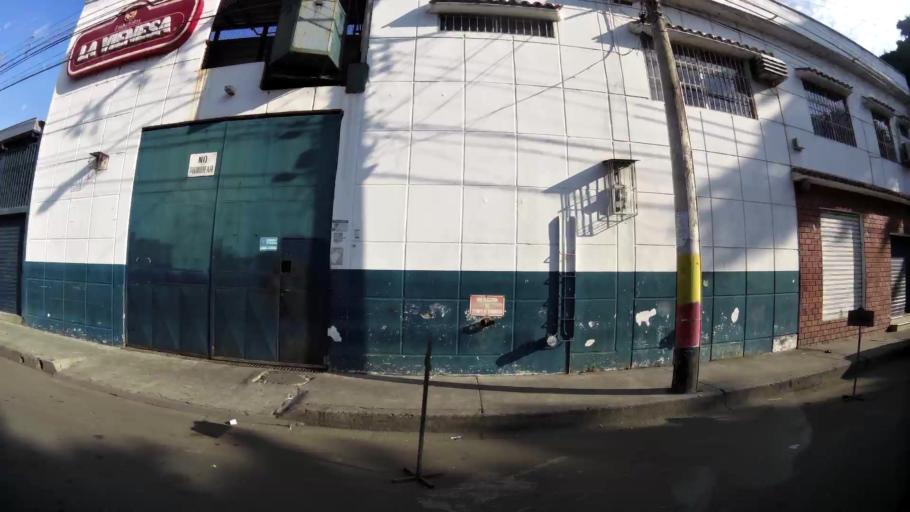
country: EC
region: Guayas
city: Guayaquil
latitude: -2.2252
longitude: -79.9053
